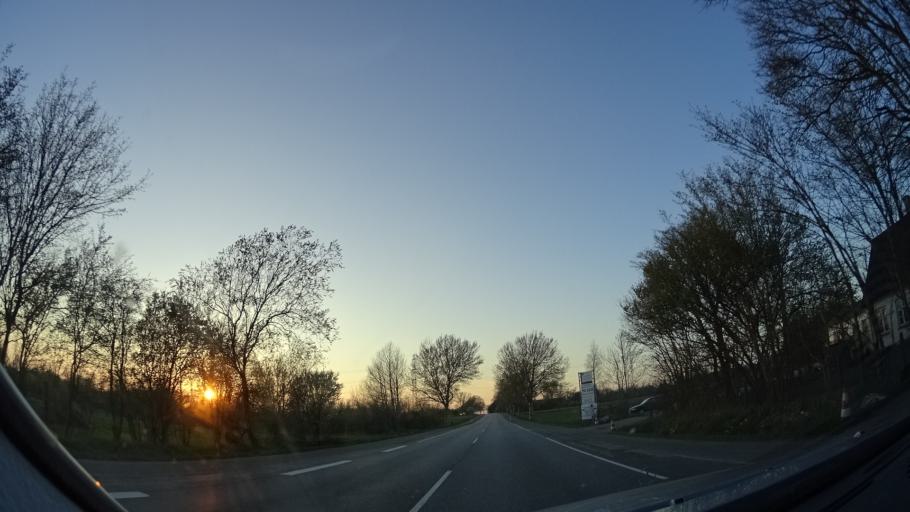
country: DK
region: Zealand
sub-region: Solrod Kommune
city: Solrod
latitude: 55.5461
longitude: 12.1693
